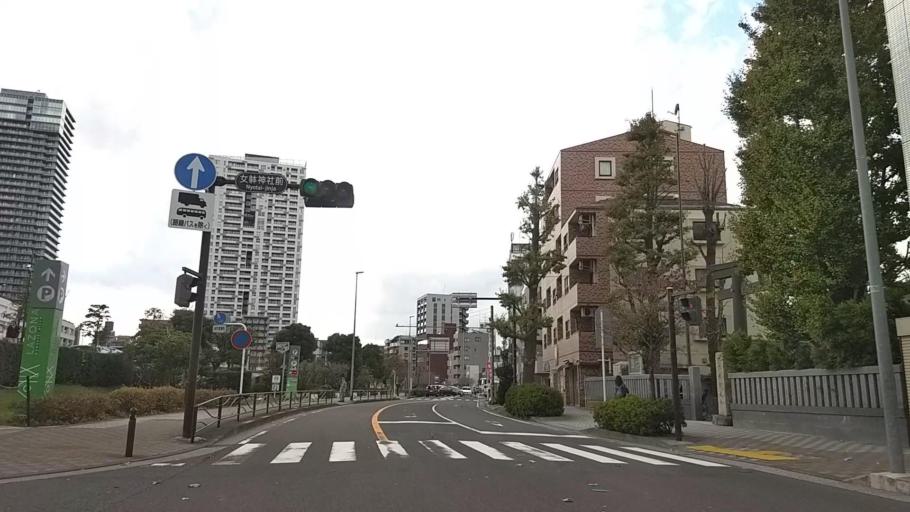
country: JP
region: Kanagawa
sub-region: Kawasaki-shi
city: Kawasaki
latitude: 35.5343
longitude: 139.6973
